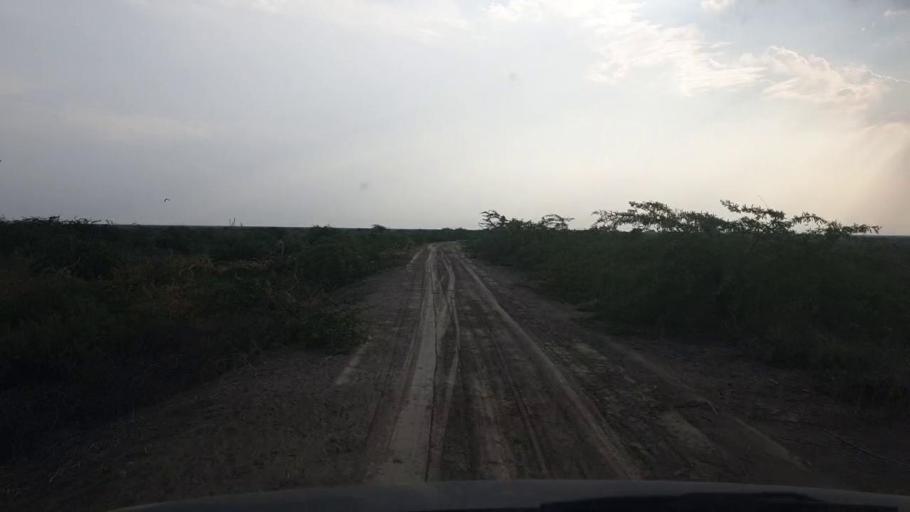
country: PK
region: Sindh
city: Badin
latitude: 24.4752
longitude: 68.6998
